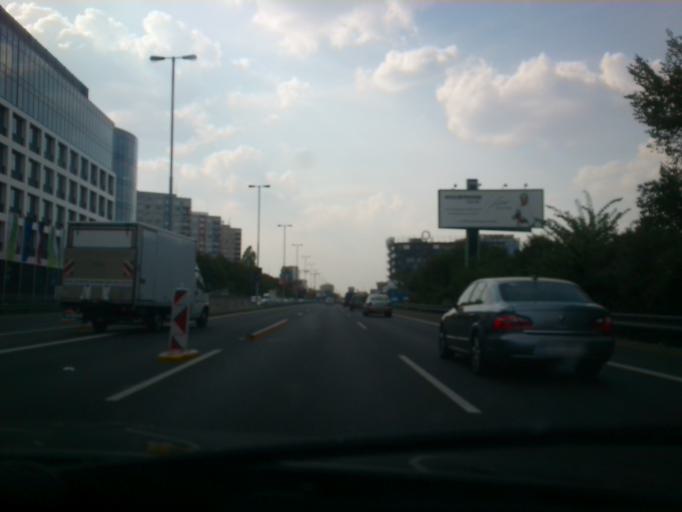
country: CZ
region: Praha
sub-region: Praha 4
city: Hodkovicky
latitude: 50.0444
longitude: 14.4597
